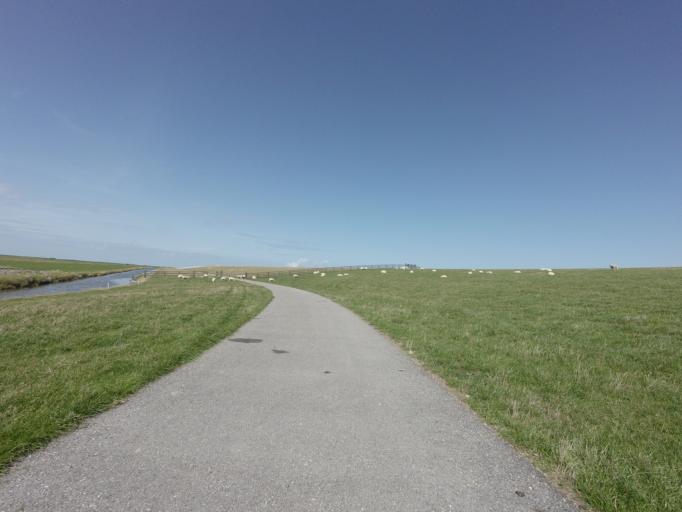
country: NL
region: Friesland
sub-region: Gemeente Dongeradeel
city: Holwerd
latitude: 53.3665
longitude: 5.8618
